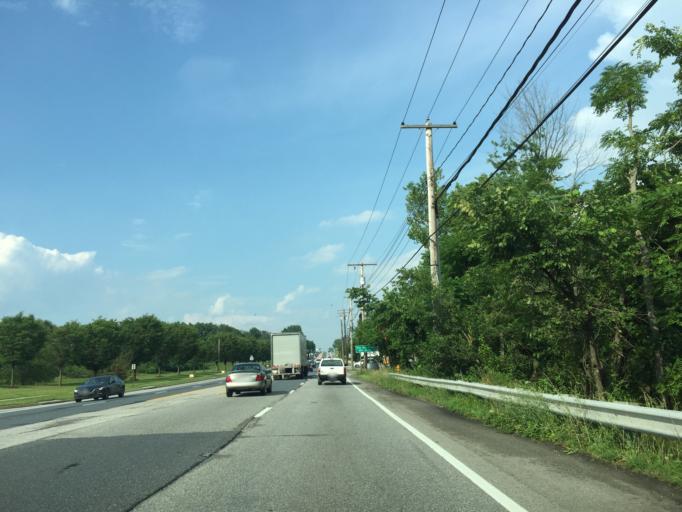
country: US
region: Maryland
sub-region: Howard County
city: Hanover
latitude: 39.1930
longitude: -76.7499
